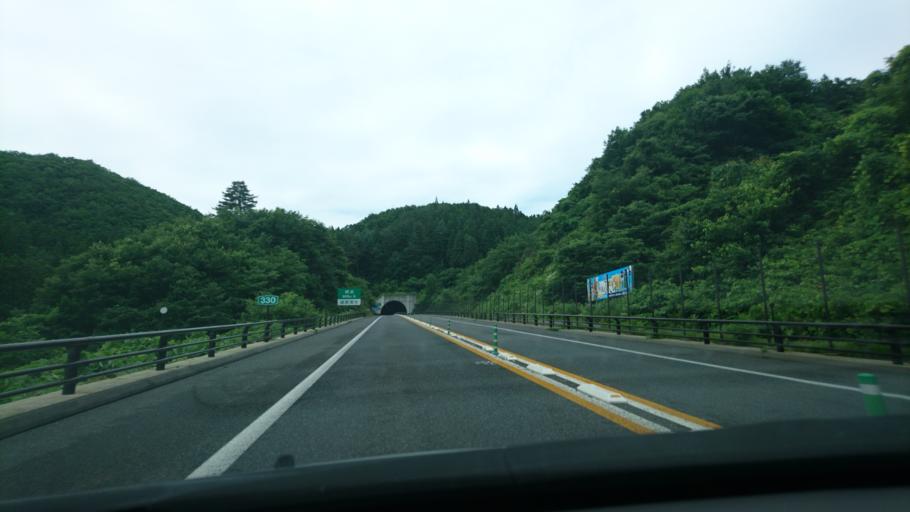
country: JP
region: Iwate
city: Miyako
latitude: 40.0145
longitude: 141.8860
